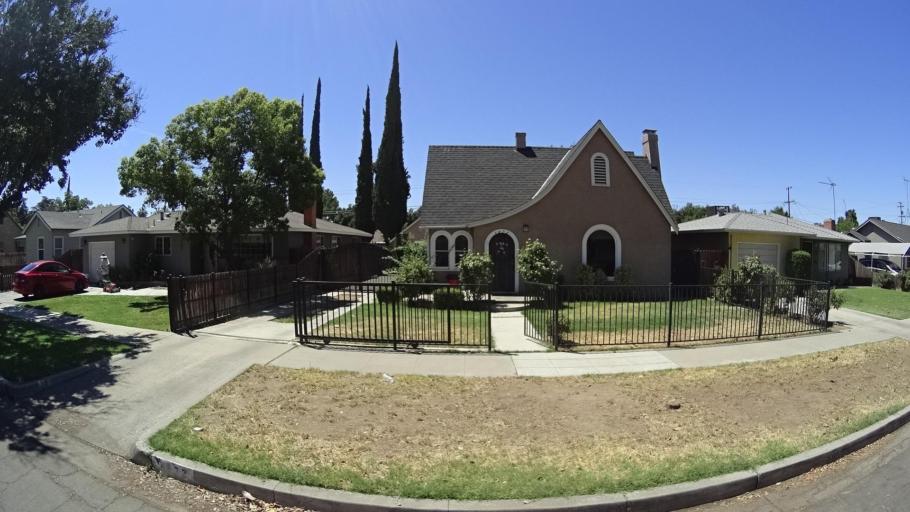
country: US
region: California
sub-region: Fresno County
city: Fresno
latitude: 36.7495
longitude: -119.7423
